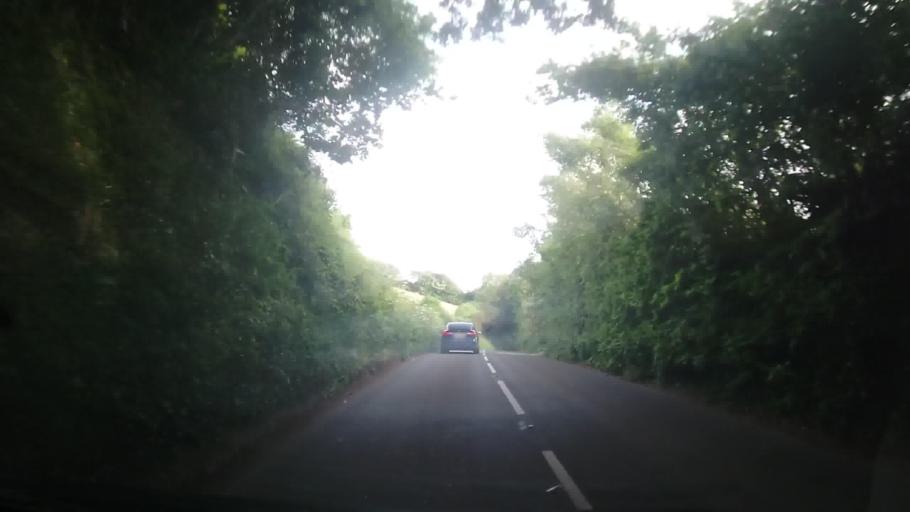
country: GB
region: England
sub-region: Devon
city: Kingsbridge
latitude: 50.2739
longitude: -3.7610
